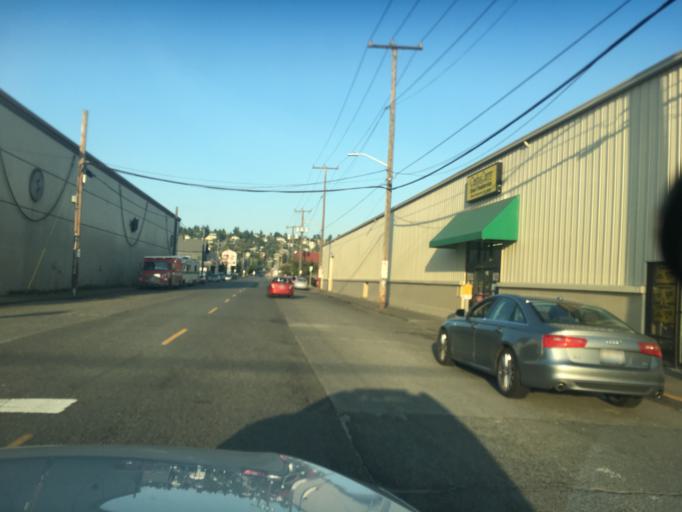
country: US
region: Washington
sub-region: King County
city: Seattle
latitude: 47.6629
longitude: -122.3736
